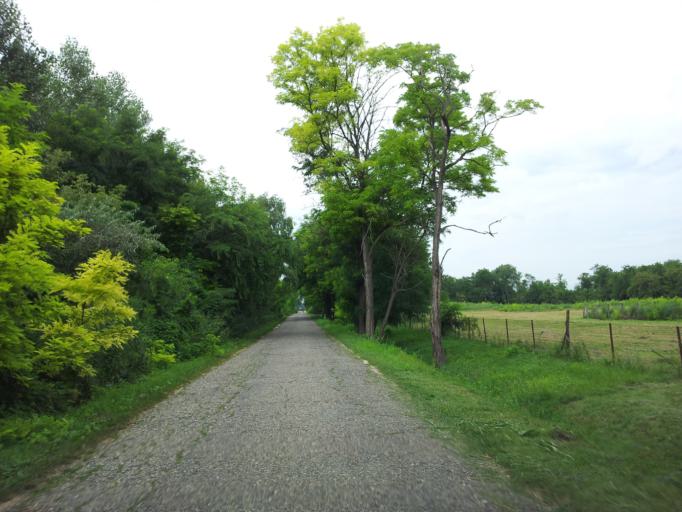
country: HU
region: Pest
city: Szigetcsep
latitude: 47.2357
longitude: 18.9891
